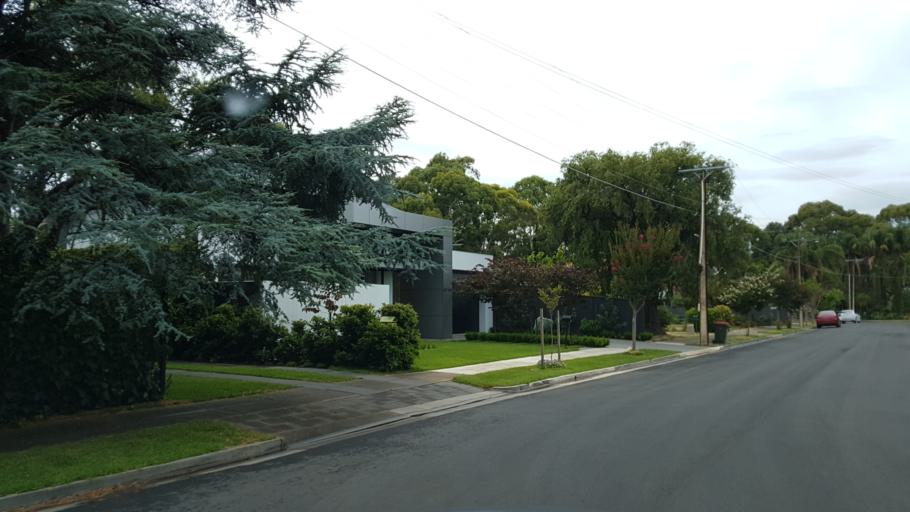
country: AU
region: South Australia
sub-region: Charles Sturt
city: Seaton
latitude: -34.9228
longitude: 138.5198
